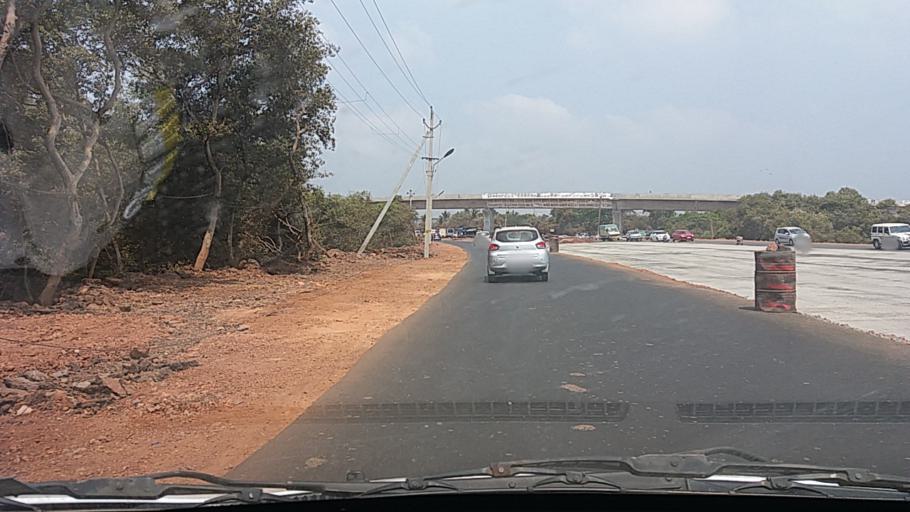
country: IN
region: Goa
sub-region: North Goa
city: Panaji
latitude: 15.4898
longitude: 73.8450
